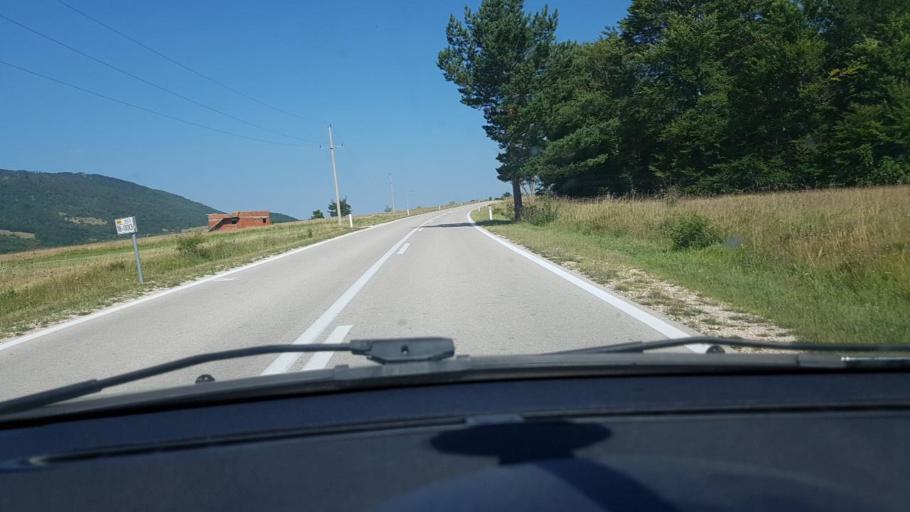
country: BA
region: Federation of Bosnia and Herzegovina
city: Bosansko Grahovo
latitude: 44.1111
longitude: 16.5436
